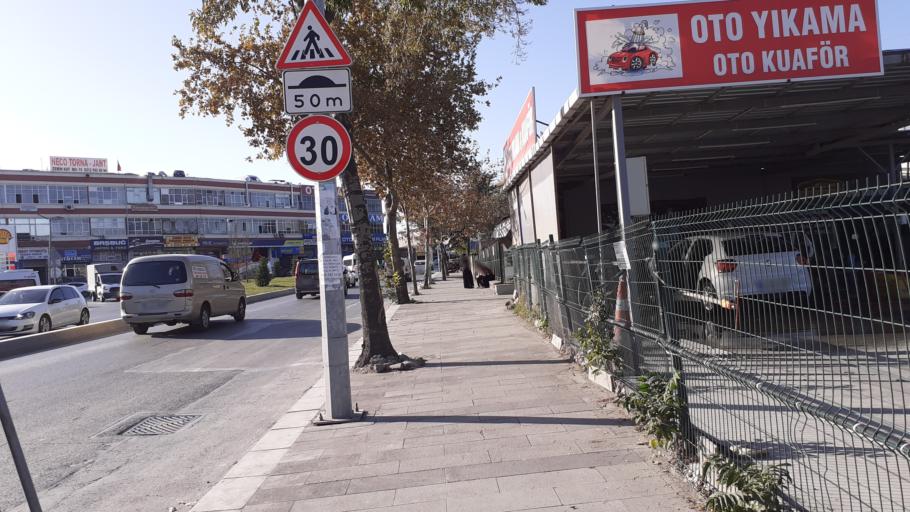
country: TR
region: Istanbul
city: Mahmutbey
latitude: 41.0103
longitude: 28.7948
